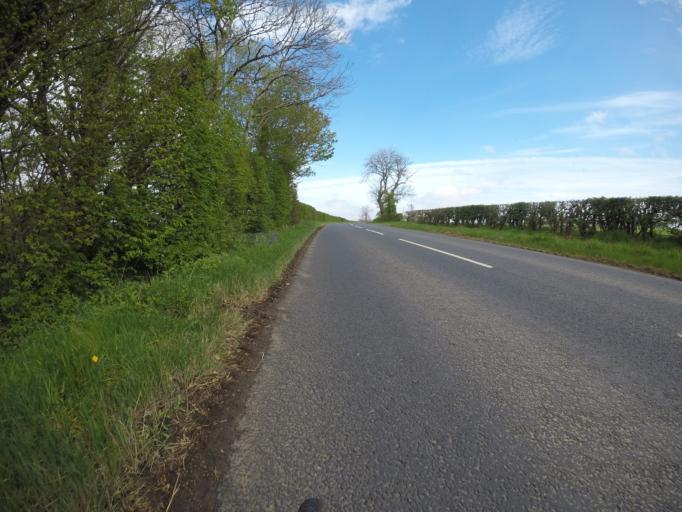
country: GB
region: Scotland
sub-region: East Ayrshire
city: Crosshouse
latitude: 55.6492
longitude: -4.5706
